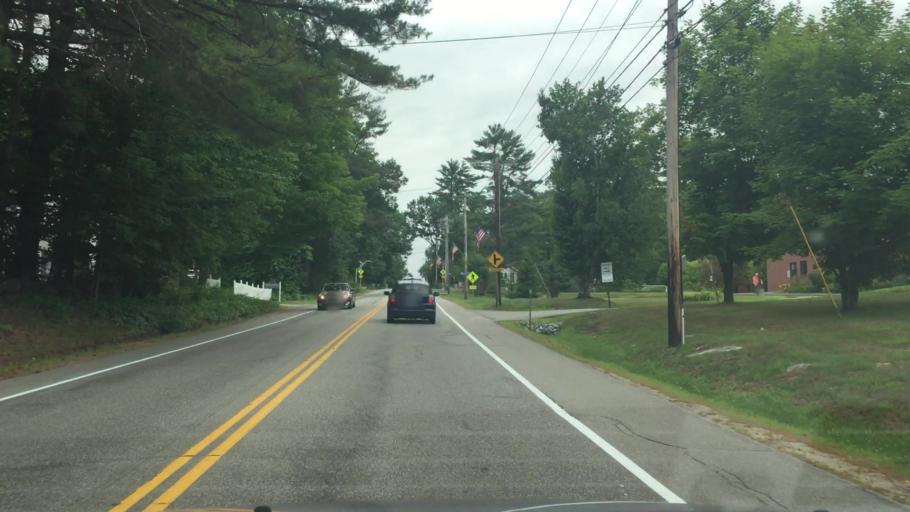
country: US
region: New Hampshire
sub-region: Carroll County
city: Moultonborough
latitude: 43.7493
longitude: -71.4022
